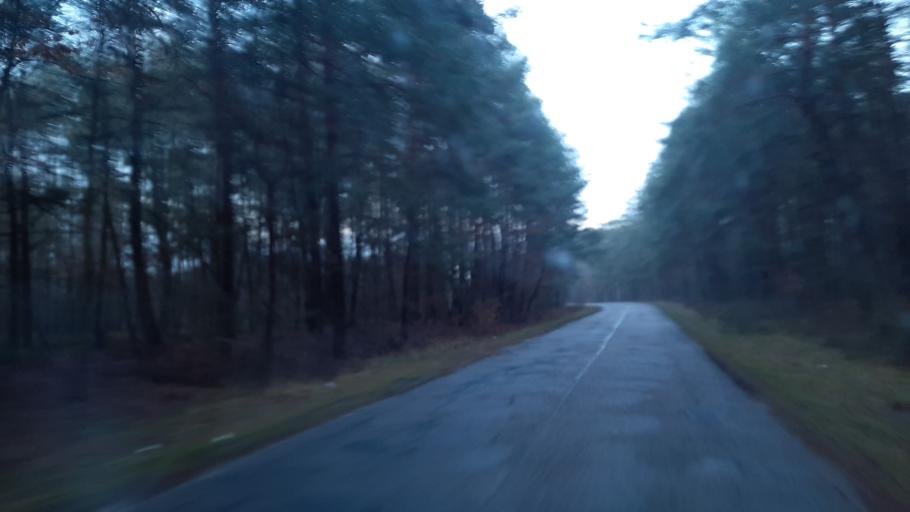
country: PL
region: Lublin Voivodeship
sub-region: Powiat lubartowski
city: Kamionka
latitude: 51.4898
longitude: 22.4816
